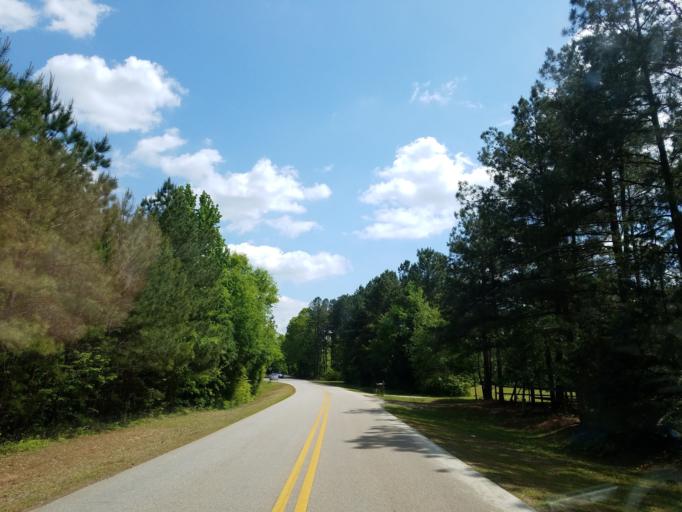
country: US
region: Georgia
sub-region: Monroe County
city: Forsyth
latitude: 33.0898
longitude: -83.9609
